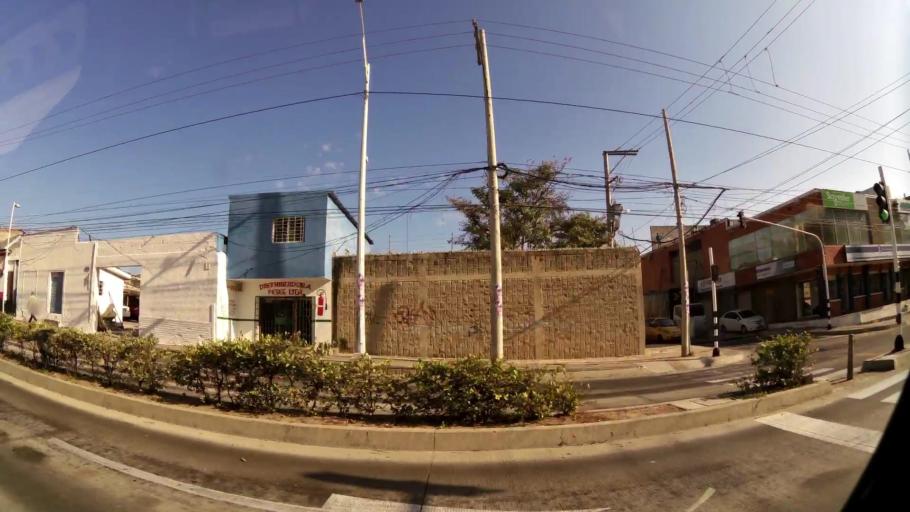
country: CO
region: Atlantico
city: Barranquilla
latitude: 10.9863
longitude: -74.7812
